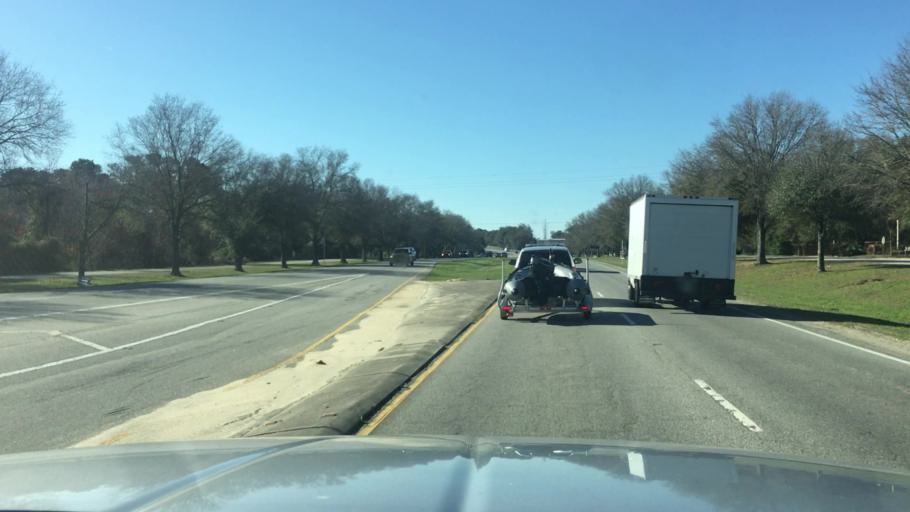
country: US
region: North Carolina
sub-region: New Hanover County
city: Sea Breeze
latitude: 34.0641
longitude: -77.8985
